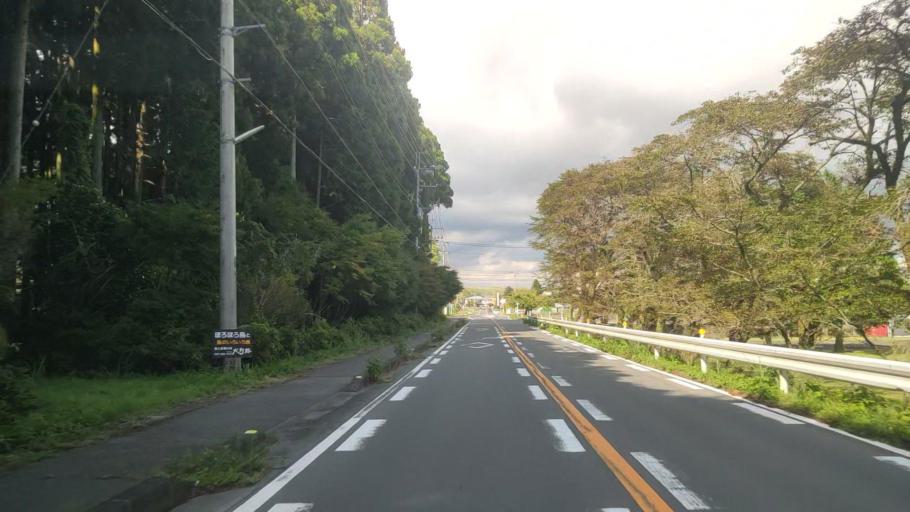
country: JP
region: Shizuoka
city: Gotemba
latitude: 35.2566
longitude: 138.8590
